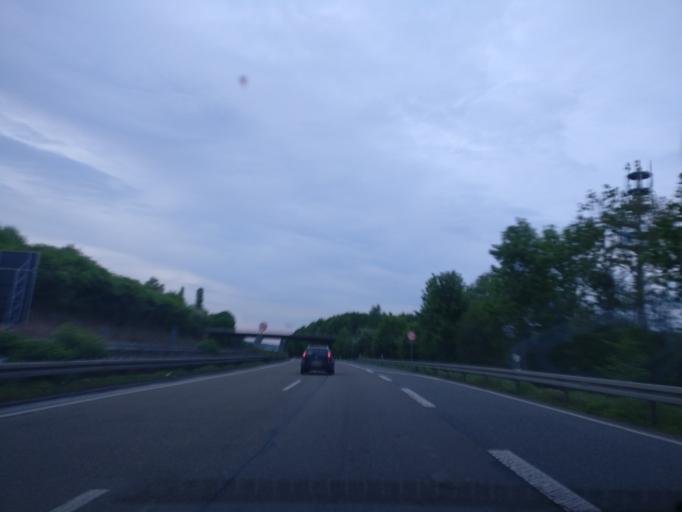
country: DE
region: Hesse
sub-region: Regierungsbezirk Kassel
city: Baunatal
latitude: 51.2301
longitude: 9.4262
